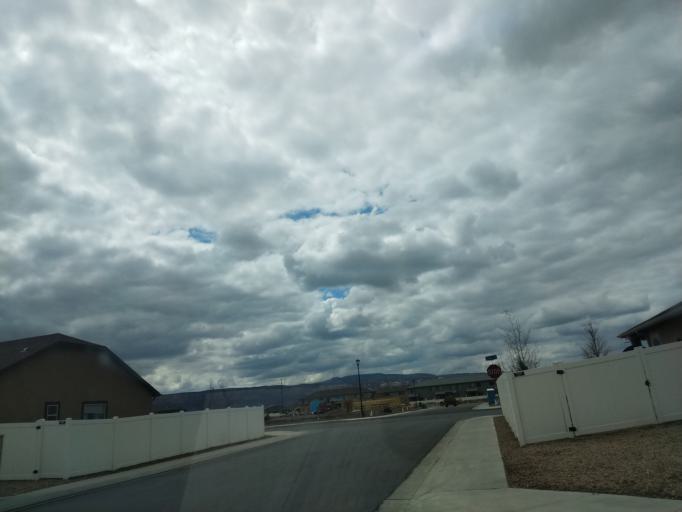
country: US
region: Colorado
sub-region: Mesa County
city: Redlands
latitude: 39.1007
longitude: -108.5936
